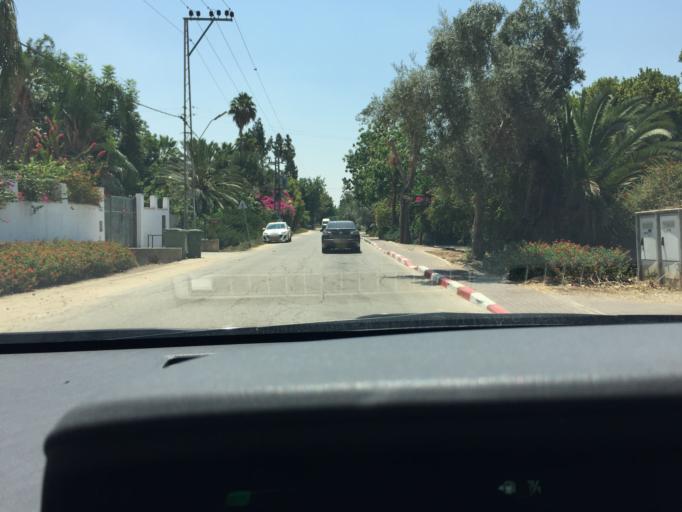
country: IL
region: Central District
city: Nehalim
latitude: 32.0506
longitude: 34.9023
